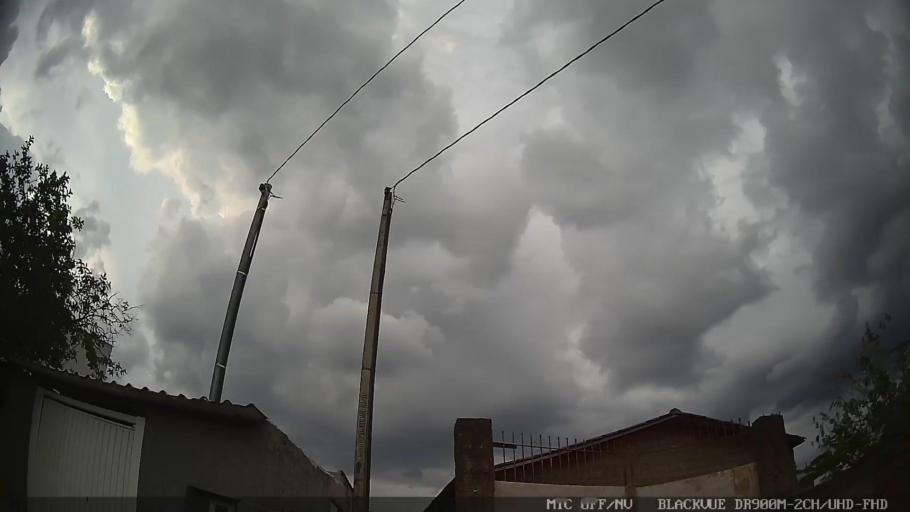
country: BR
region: Sao Paulo
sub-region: Braganca Paulista
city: Braganca Paulista
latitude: -22.9113
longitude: -46.5190
